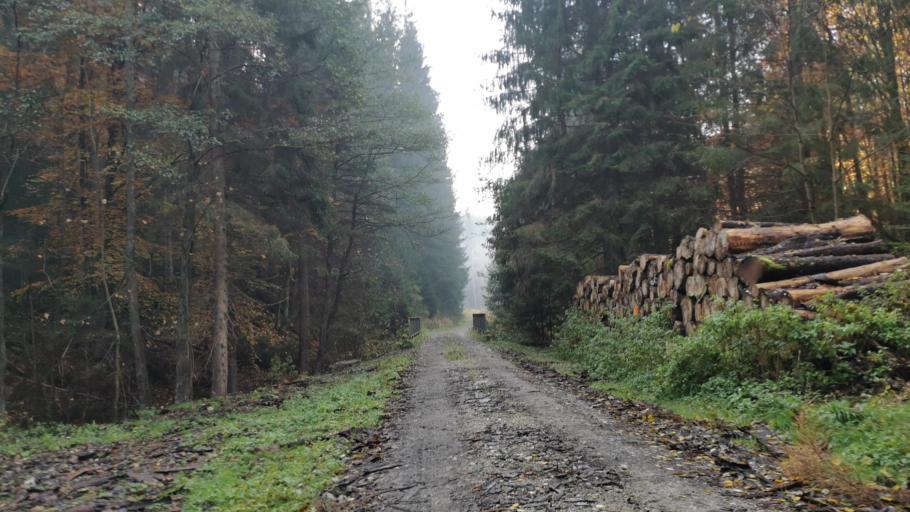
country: DE
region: Bavaria
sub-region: Upper Franconia
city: Nordhalben
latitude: 50.3979
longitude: 11.5383
